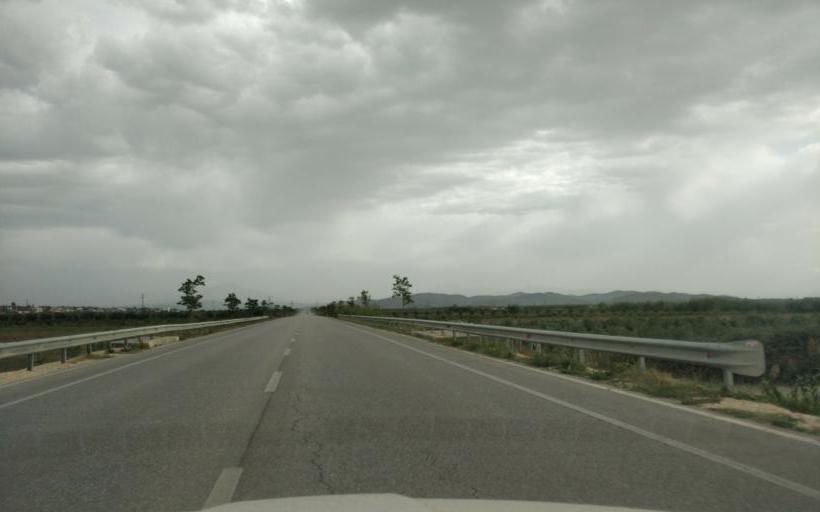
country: AL
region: Fier
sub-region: Rrethi i Fierit
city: Frakulla e Madhe
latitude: 40.6494
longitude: 19.4957
